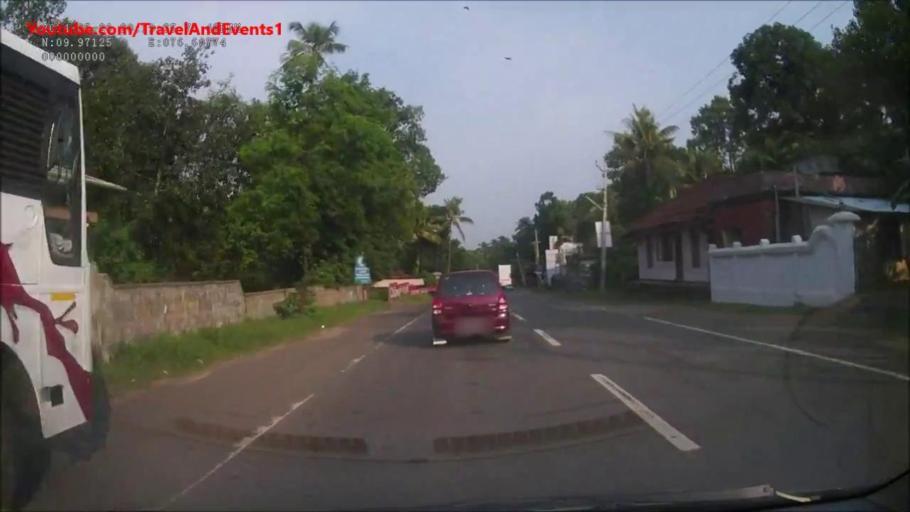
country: IN
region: Kerala
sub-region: Ernakulam
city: Muvattupula
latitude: 9.9615
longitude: 76.6187
